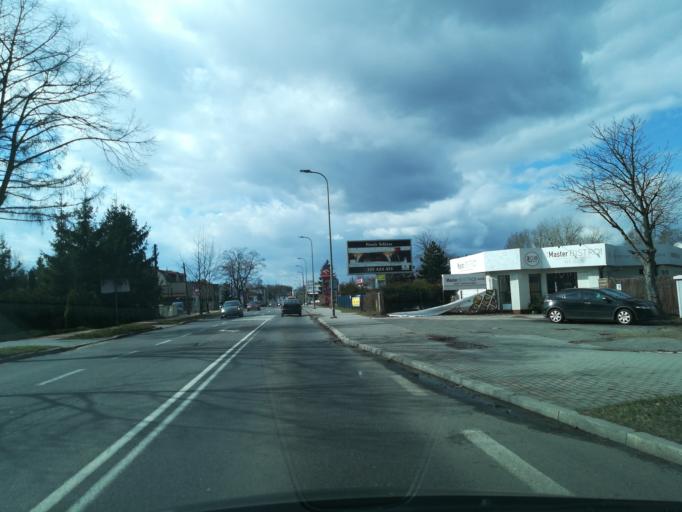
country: PL
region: Silesian Voivodeship
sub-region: Dabrowa Gornicza
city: Dabrowa Gornicza
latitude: 50.3181
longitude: 19.1940
